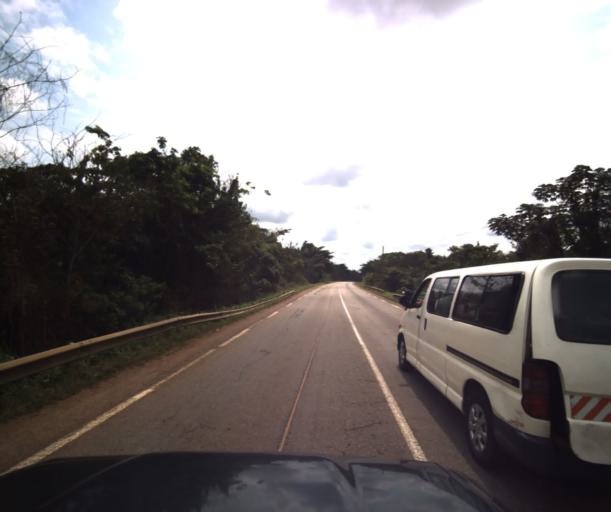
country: CM
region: Centre
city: Eseka
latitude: 3.8579
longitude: 10.5611
